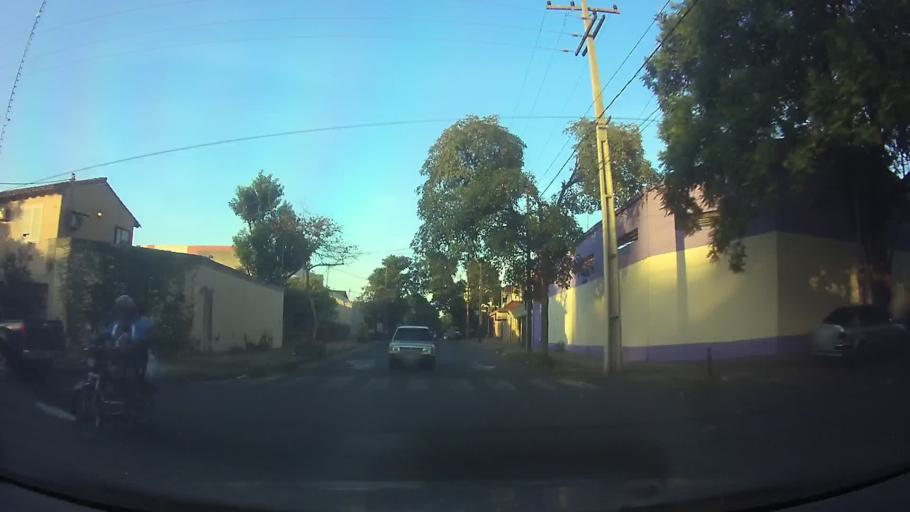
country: PY
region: Central
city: Lambare
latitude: -25.3110
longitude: -57.5792
